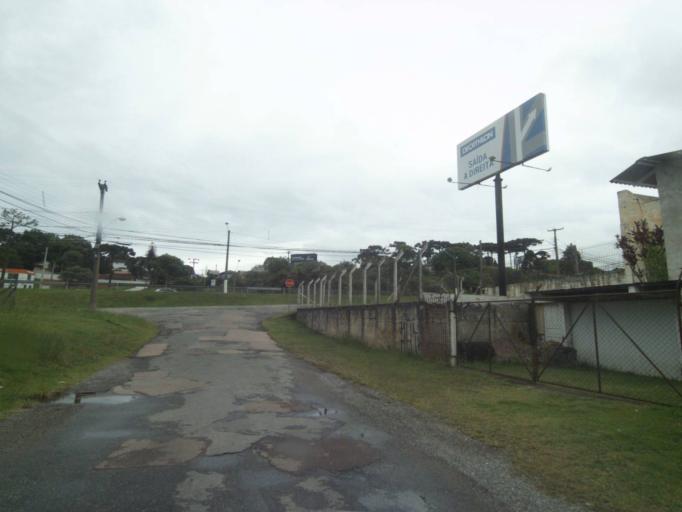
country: BR
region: Parana
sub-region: Curitiba
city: Curitiba
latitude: -25.4295
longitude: -49.3204
